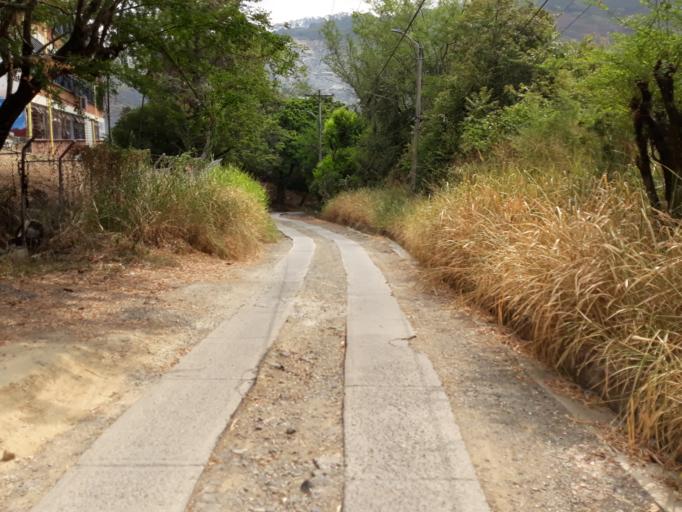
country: CO
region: Valle del Cauca
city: Cali
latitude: 3.4617
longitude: -76.5606
